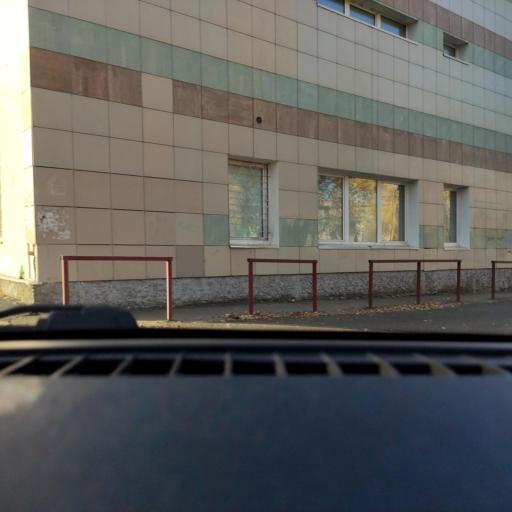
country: RU
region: Perm
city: Perm
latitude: 58.0015
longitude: 56.2877
